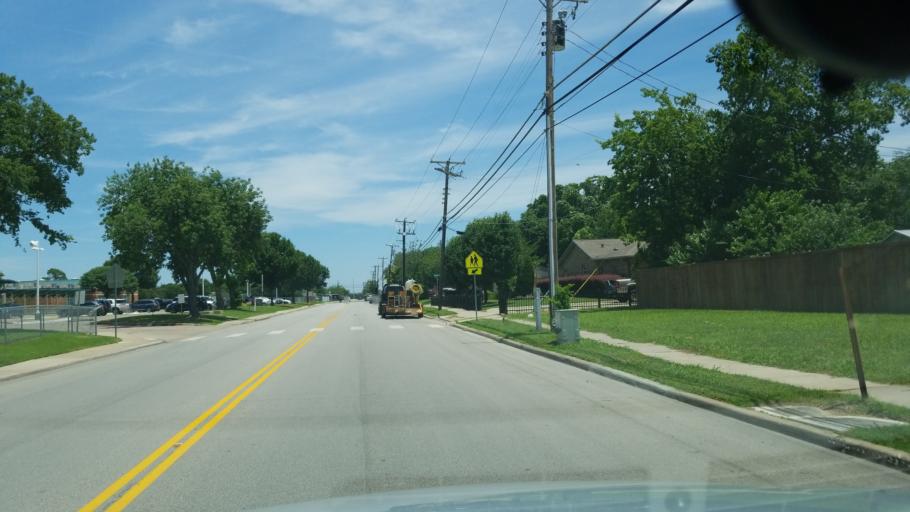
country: US
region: Texas
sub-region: Dallas County
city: Irving
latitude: 32.8176
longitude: -96.9290
